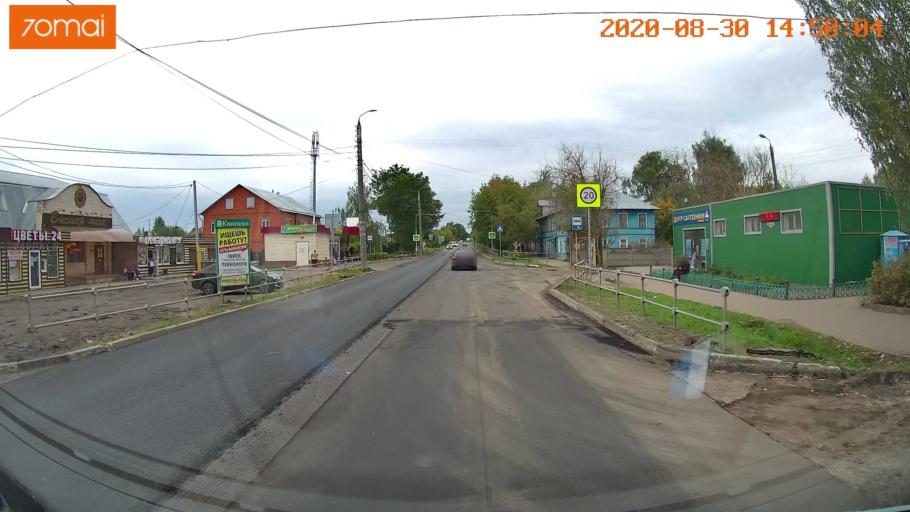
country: RU
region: Ivanovo
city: Kineshma
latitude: 57.4302
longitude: 42.0997
